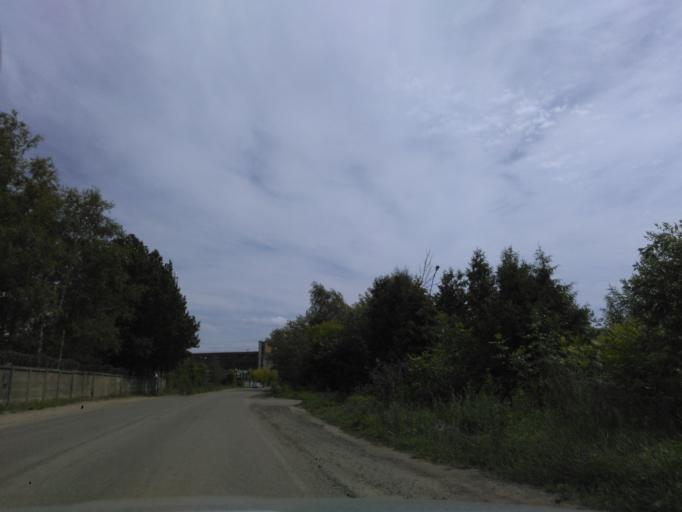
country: RU
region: Moskovskaya
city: Solnechnogorsk
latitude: 56.1705
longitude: 36.9809
